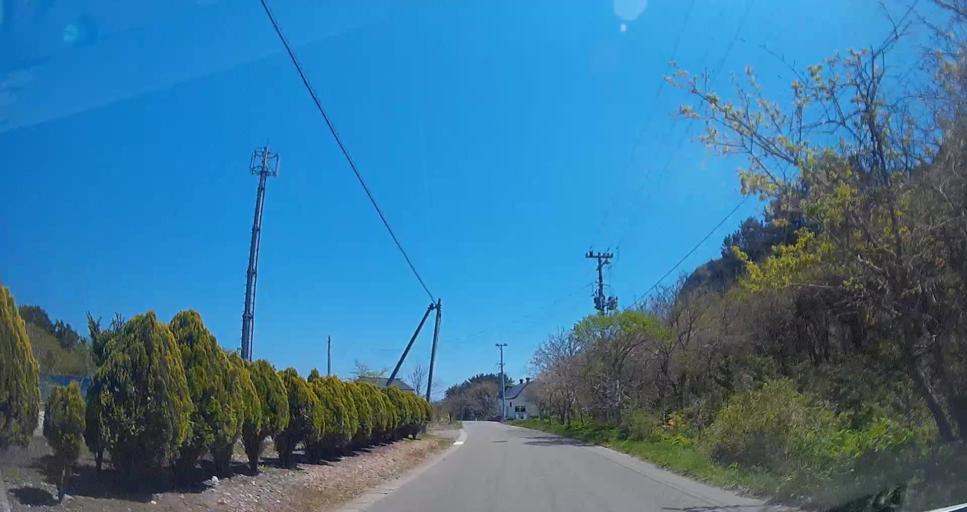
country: JP
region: Aomori
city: Mutsu
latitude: 41.3977
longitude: 141.4499
